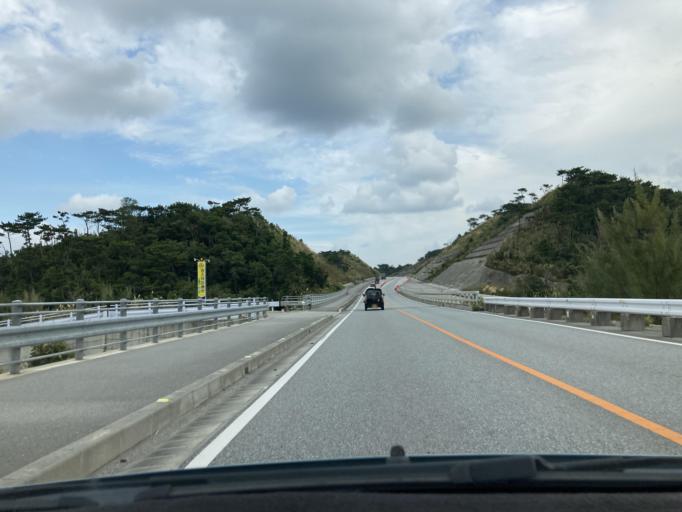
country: JP
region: Okinawa
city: Ishikawa
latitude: 26.4686
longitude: 127.8331
